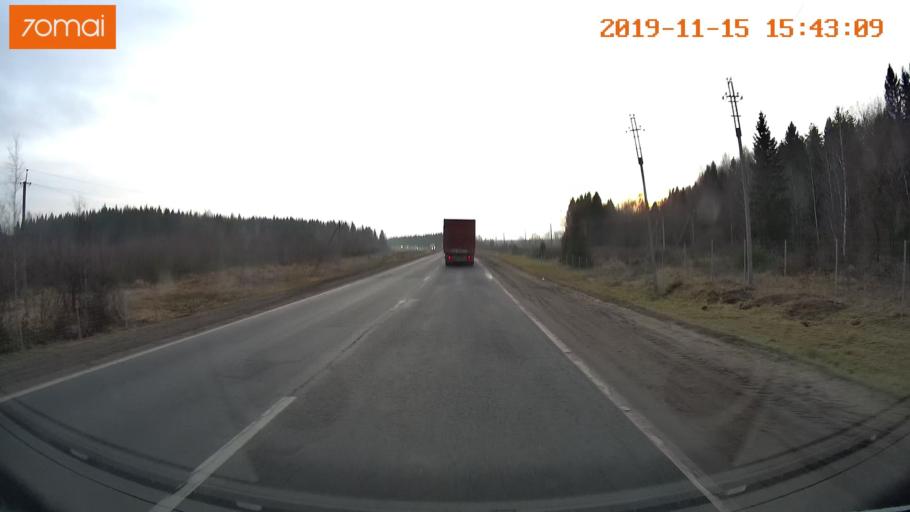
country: RU
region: Jaroslavl
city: Danilov
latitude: 57.9857
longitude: 40.0312
